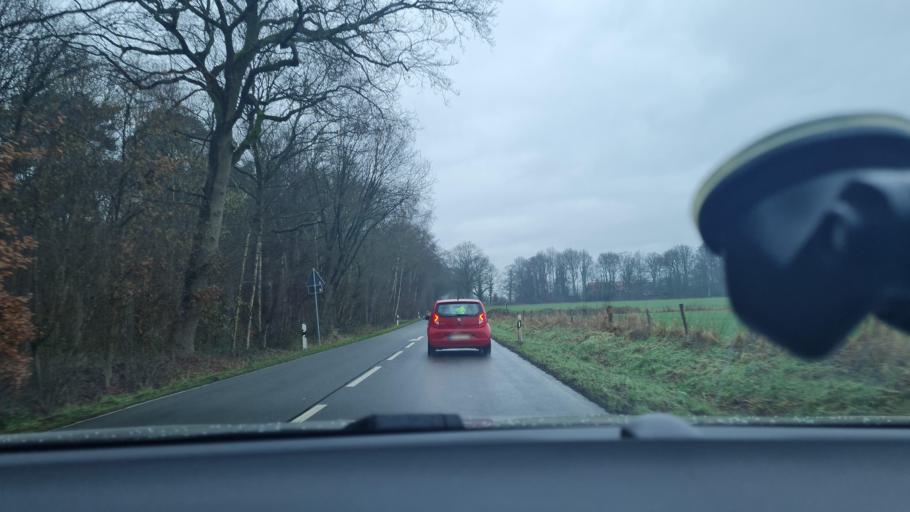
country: DE
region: North Rhine-Westphalia
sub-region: Regierungsbezirk Dusseldorf
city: Hunxe
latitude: 51.6947
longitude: 6.7462
